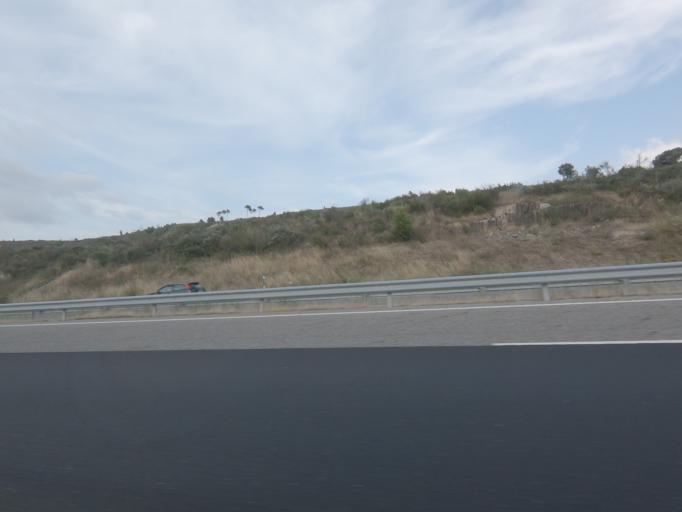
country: PT
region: Vila Real
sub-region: Boticas
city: Boticas
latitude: 41.6270
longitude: -7.5959
